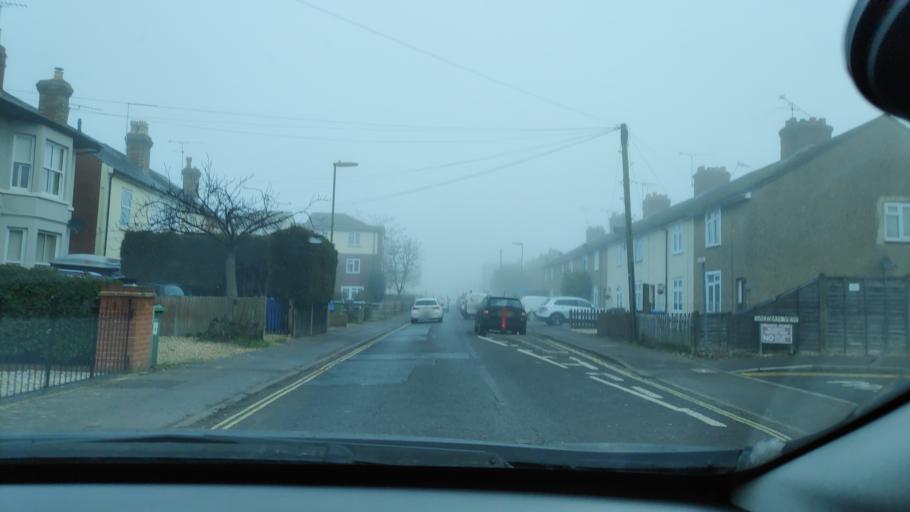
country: GB
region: England
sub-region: Hampshire
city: Farnborough
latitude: 51.2764
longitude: -0.7377
